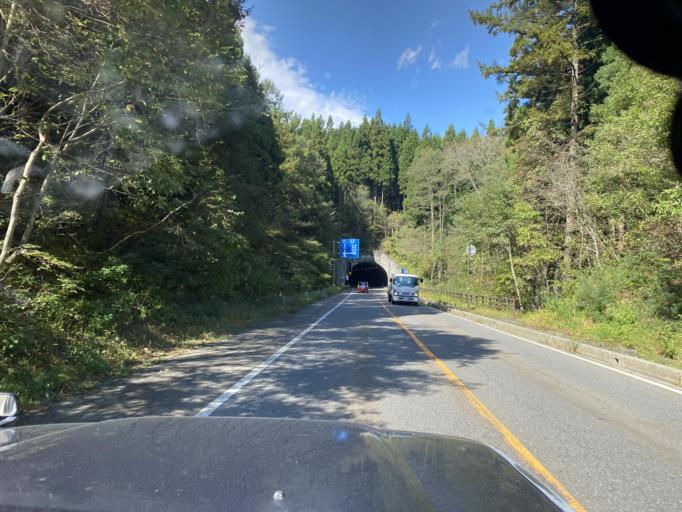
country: JP
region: Nagano
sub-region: Kitaazumi Gun
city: Hakuba
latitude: 36.6194
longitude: 137.8606
